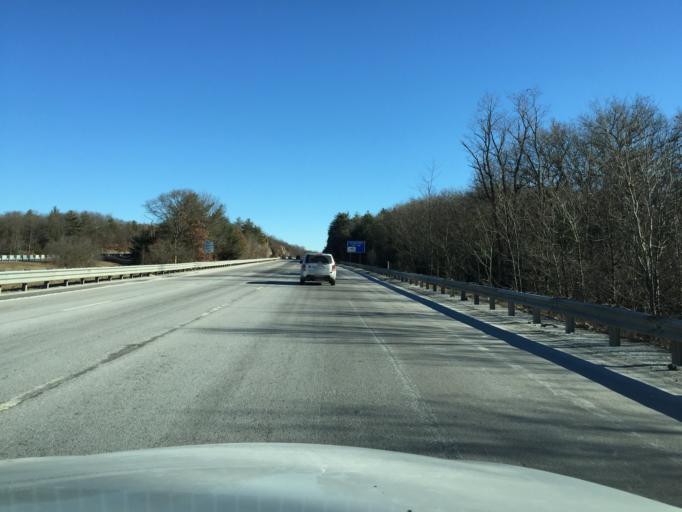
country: US
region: Massachusetts
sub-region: Norfolk County
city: Wrentham
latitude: 42.0399
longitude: -71.3447
